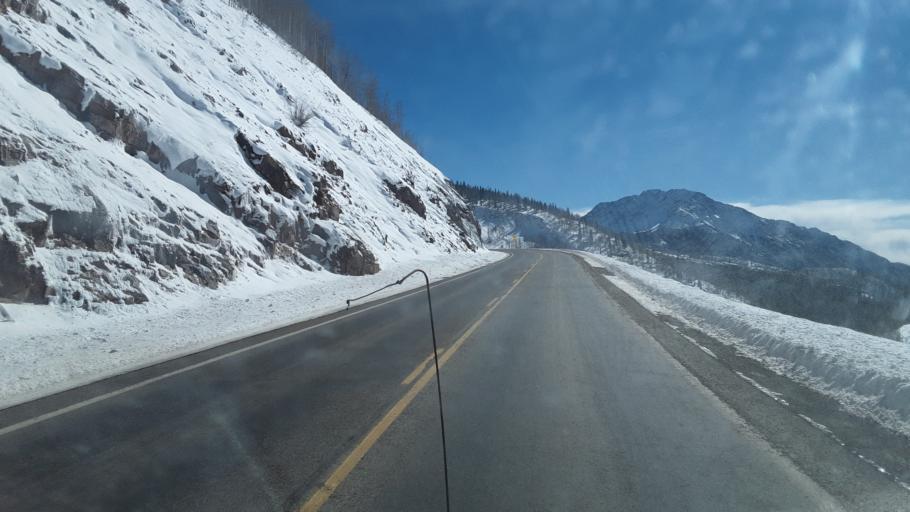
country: US
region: Colorado
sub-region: San Juan County
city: Silverton
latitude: 37.7304
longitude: -107.7491
